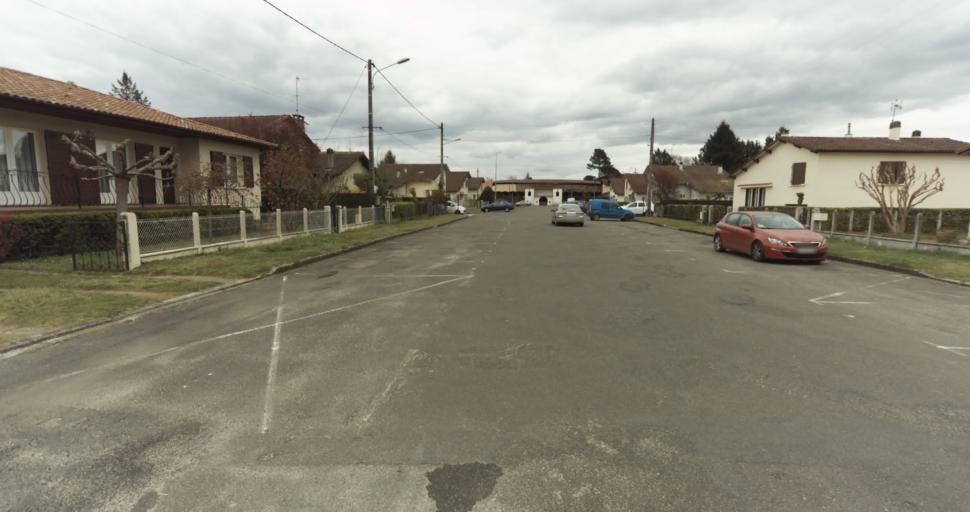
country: FR
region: Aquitaine
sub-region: Departement des Landes
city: Roquefort
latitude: 44.0337
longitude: -0.3188
